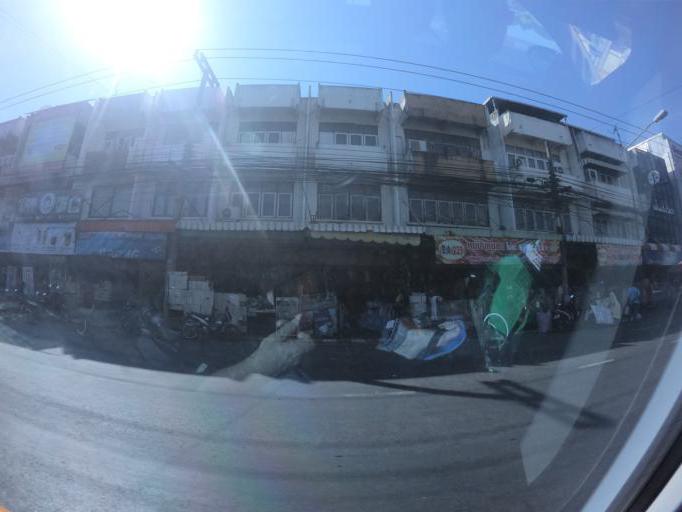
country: TH
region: Khon Kaen
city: Khon Kaen
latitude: 16.4275
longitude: 102.8352
